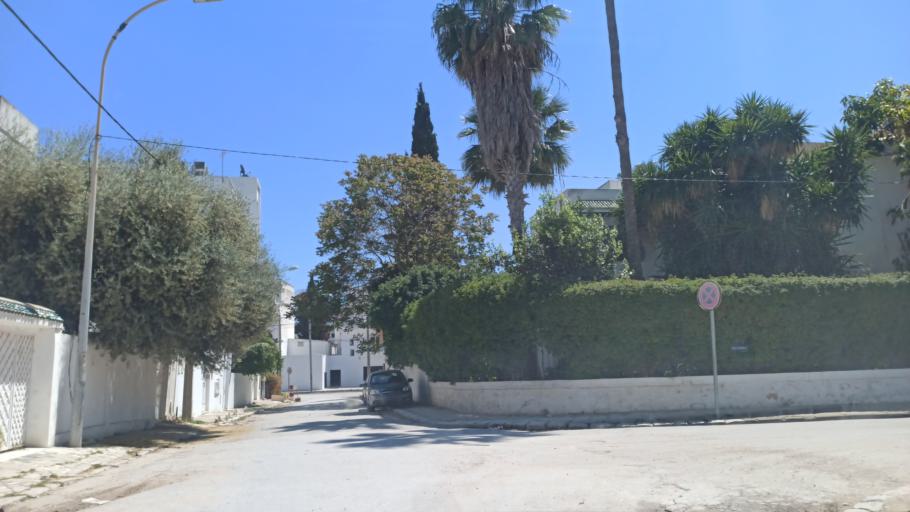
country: TN
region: Tunis
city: Tunis
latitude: 36.8212
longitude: 10.1821
